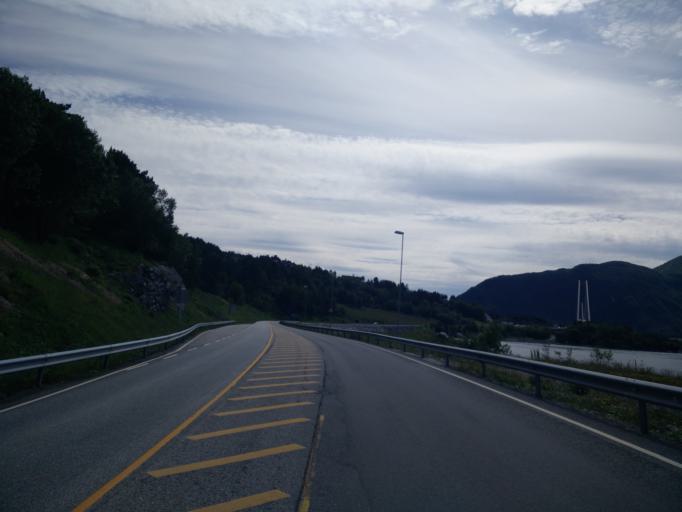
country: NO
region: More og Romsdal
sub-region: Kristiansund
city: Rensvik
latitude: 62.9812
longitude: 7.7948
